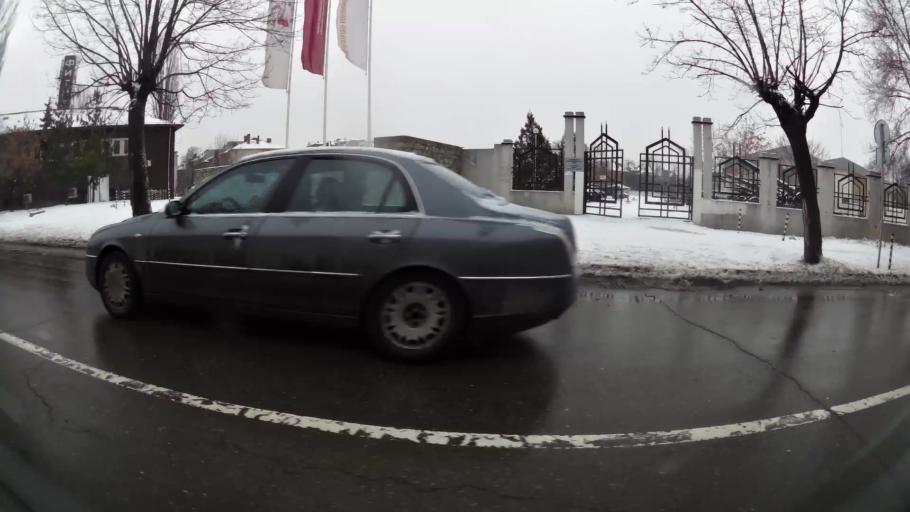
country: BG
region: Sofia-Capital
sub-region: Stolichna Obshtina
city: Sofia
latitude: 42.6877
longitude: 23.3517
